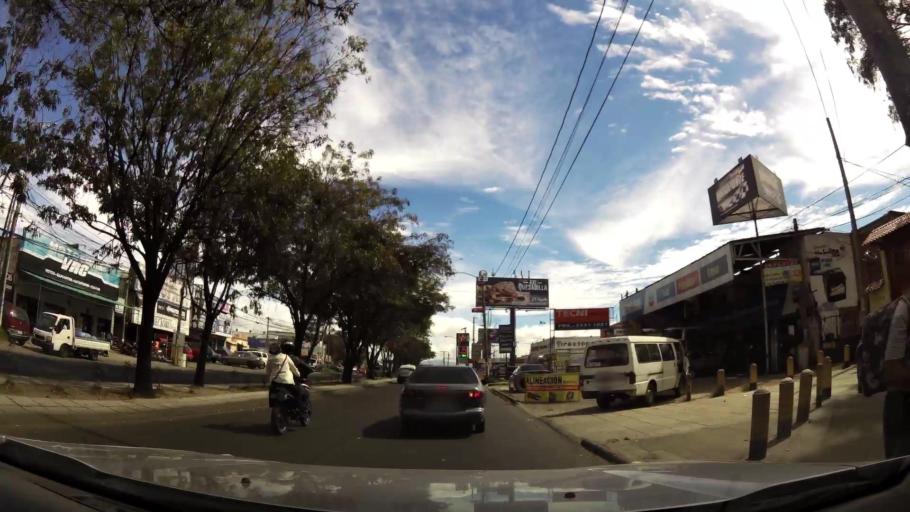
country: GT
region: Guatemala
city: Mixco
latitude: 14.6474
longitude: -90.5808
